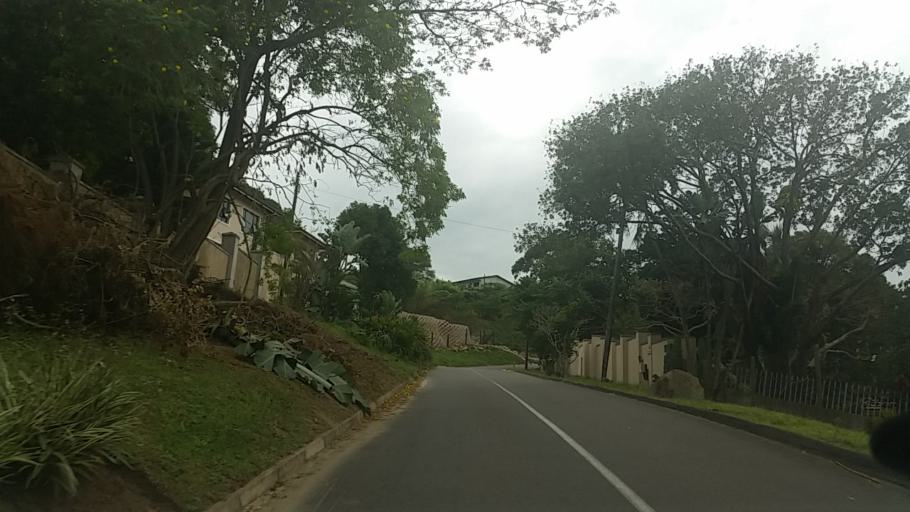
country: ZA
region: KwaZulu-Natal
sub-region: eThekwini Metropolitan Municipality
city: Berea
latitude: -29.8400
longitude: 30.9354
